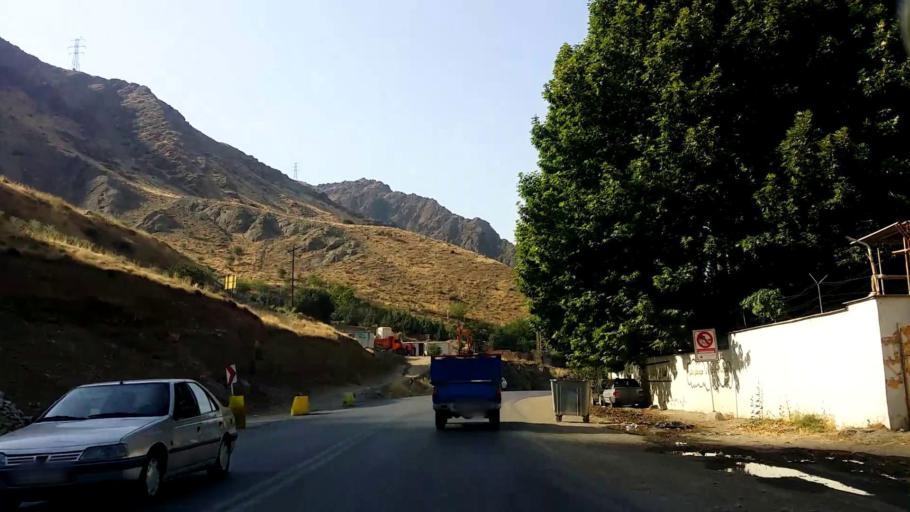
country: IR
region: Alborz
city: Karaj
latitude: 35.9037
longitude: 51.0441
